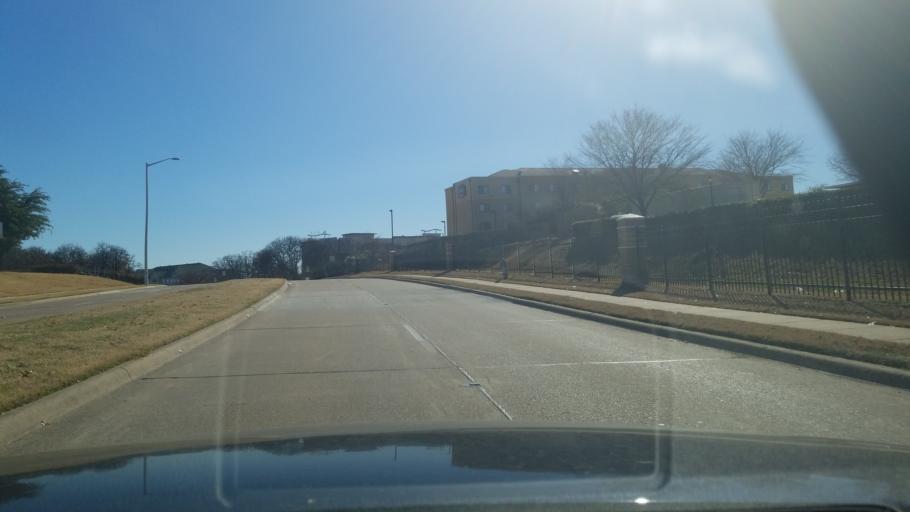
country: US
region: Texas
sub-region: Denton County
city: Denton
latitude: 33.1850
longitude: -97.1006
